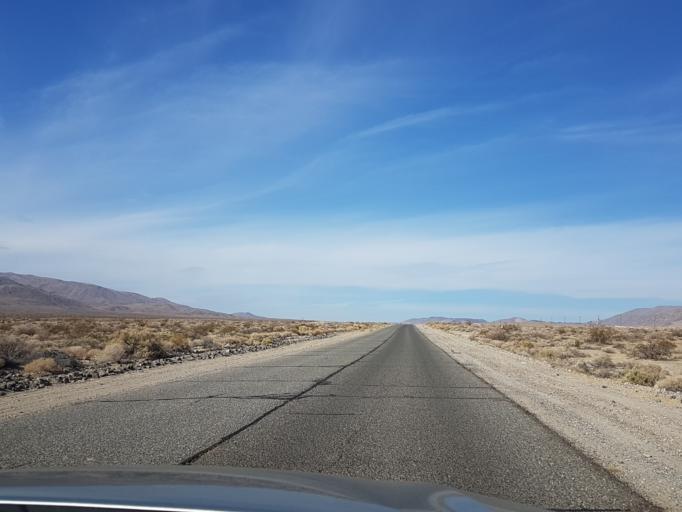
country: US
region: California
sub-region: San Bernardino County
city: Searles Valley
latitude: 35.8346
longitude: -117.3373
